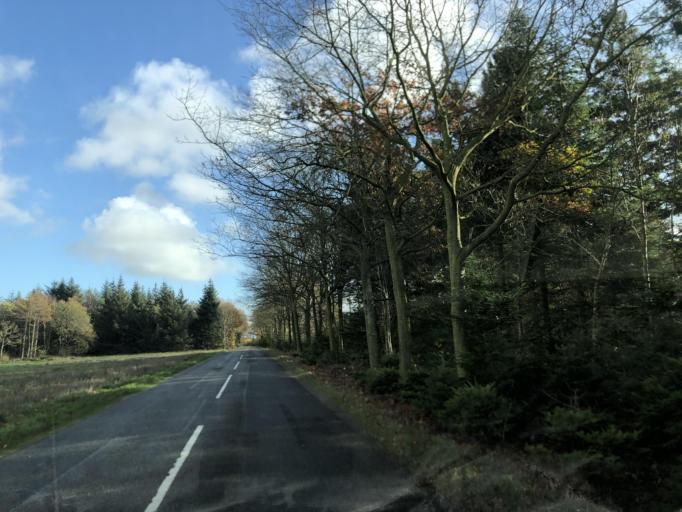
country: DK
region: Central Jutland
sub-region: Ringkobing-Skjern Kommune
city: Ringkobing
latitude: 56.1421
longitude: 8.3056
